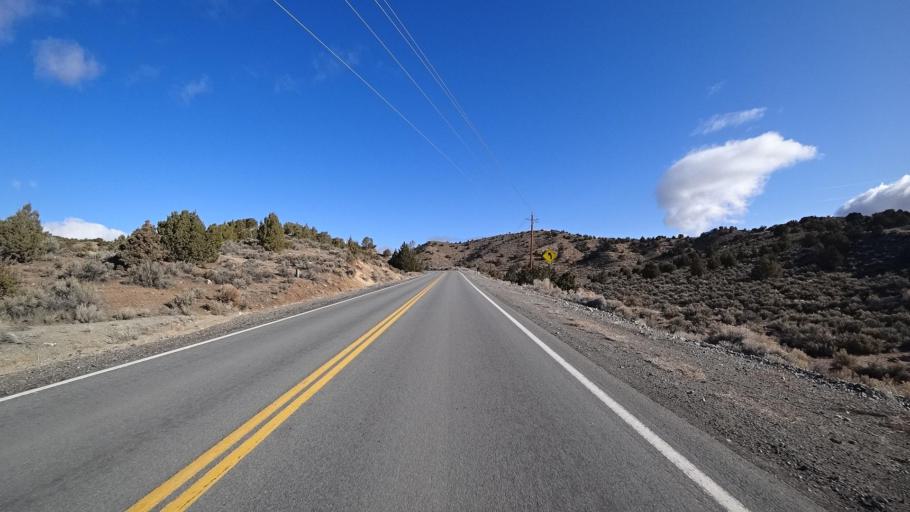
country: US
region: Nevada
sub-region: Washoe County
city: Lemmon Valley
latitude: 39.7316
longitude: -119.8811
